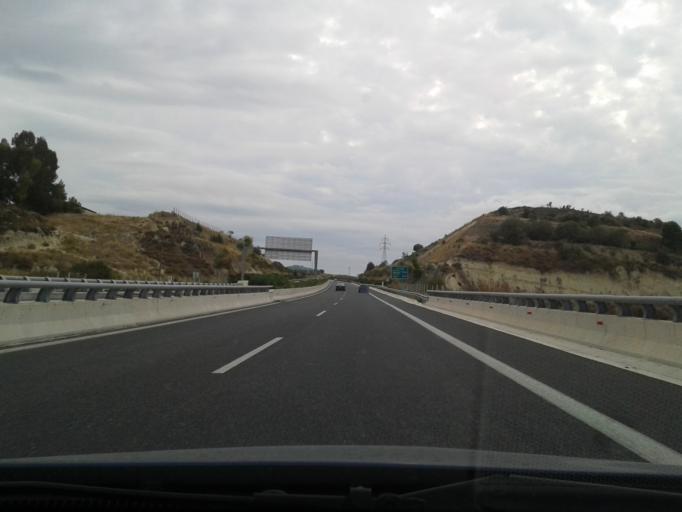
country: GR
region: Peloponnese
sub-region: Nomos Korinthias
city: Arkhaia Korinthos
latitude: 37.9114
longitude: 22.9065
